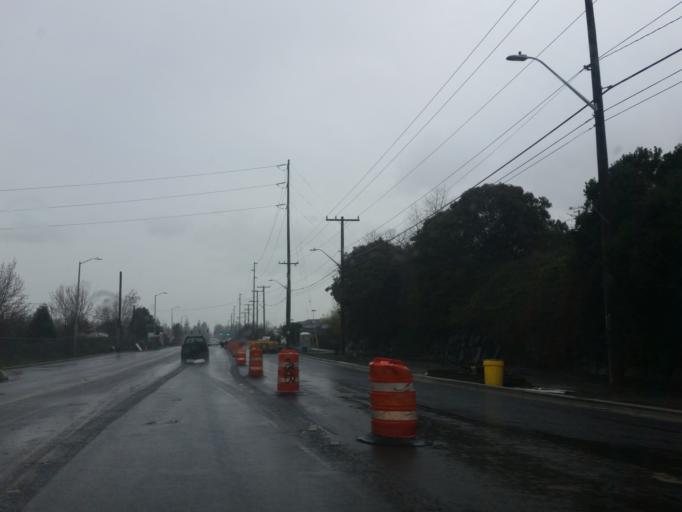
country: US
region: Washington
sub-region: King County
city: Shoreline
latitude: 47.7038
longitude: -122.3286
